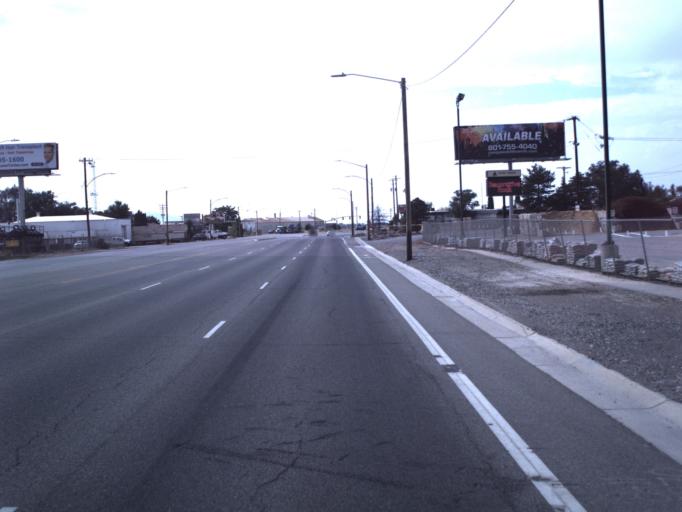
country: US
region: Utah
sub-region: Davis County
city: North Salt Lake
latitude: 40.8034
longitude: -111.9146
